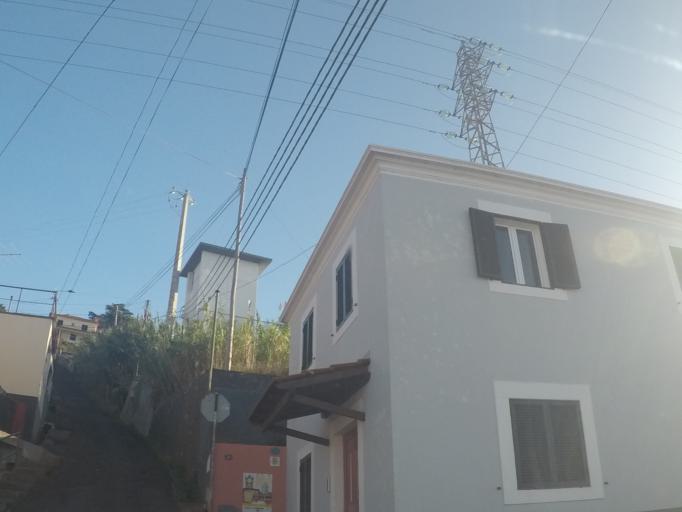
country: PT
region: Madeira
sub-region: Funchal
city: Nossa Senhora do Monte
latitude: 32.6650
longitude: -16.8885
